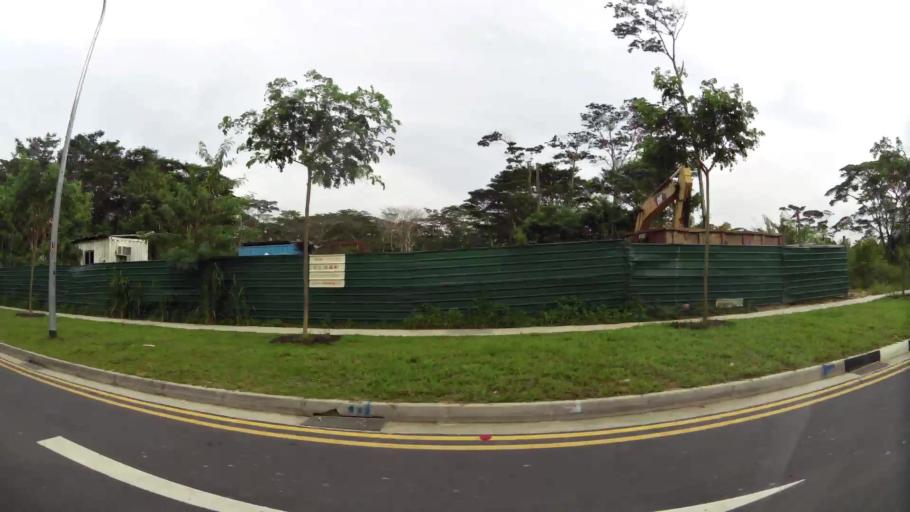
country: MY
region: Johor
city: Kampung Pasir Gudang Baru
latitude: 1.4135
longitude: 103.9012
